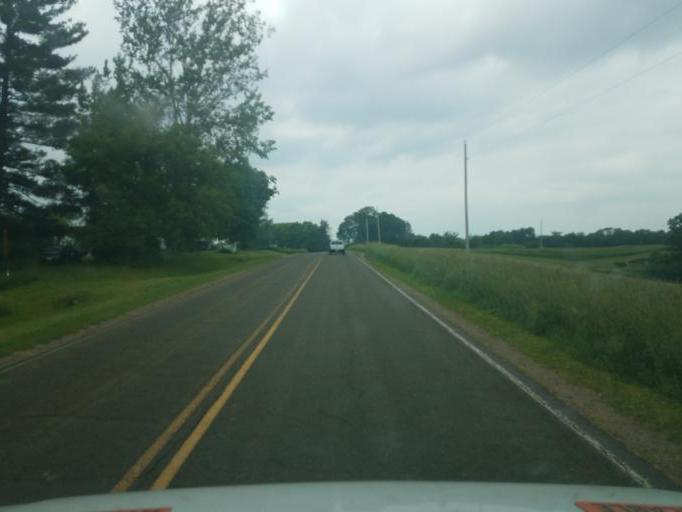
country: US
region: Wisconsin
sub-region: Vernon County
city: Hillsboro
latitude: 43.6477
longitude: -90.2645
